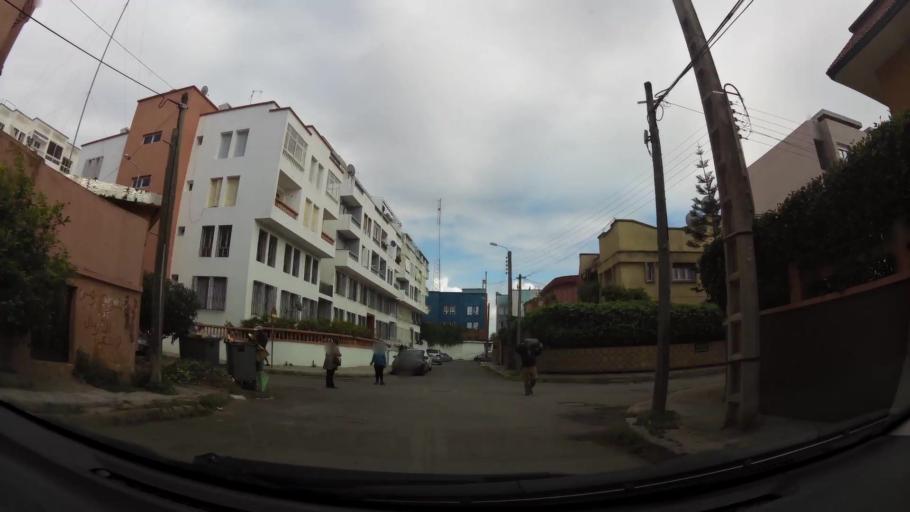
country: MA
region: Doukkala-Abda
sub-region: El-Jadida
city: El Jadida
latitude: 33.2450
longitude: -8.4962
